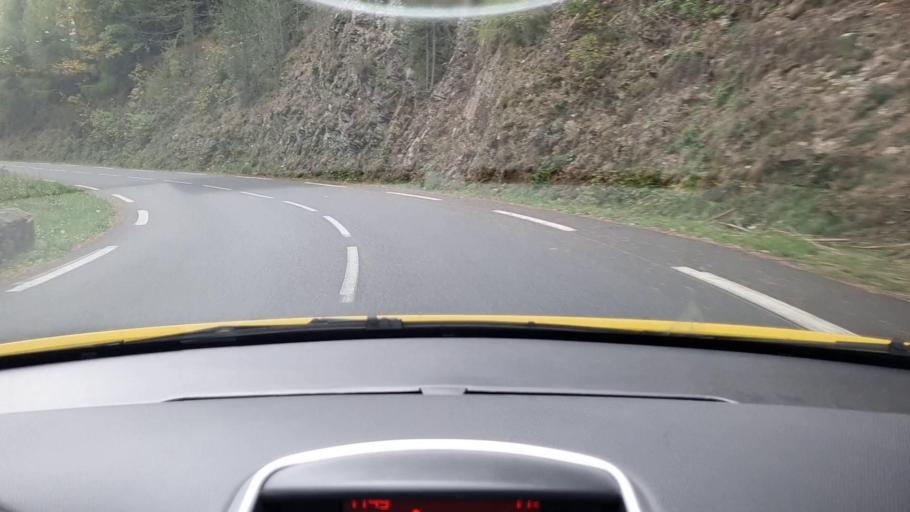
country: FR
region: Languedoc-Roussillon
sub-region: Departement de la Lozere
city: Meyrueis
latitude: 44.1320
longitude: 3.4227
